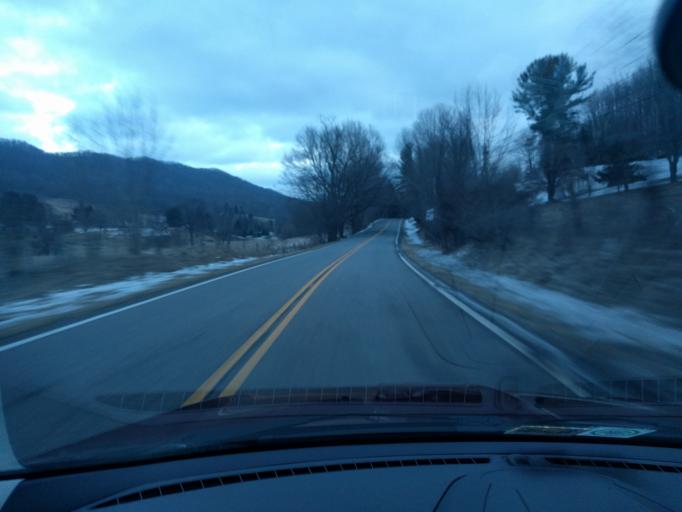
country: US
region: Virginia
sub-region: Alleghany County
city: Clifton Forge
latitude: 37.9219
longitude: -79.8903
